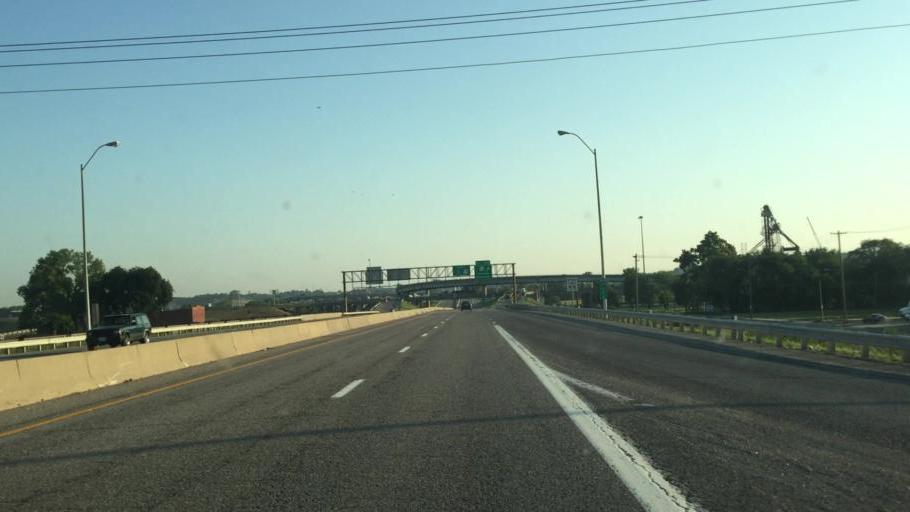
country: US
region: Kansas
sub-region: Doniphan County
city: Elwood
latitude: 39.7443
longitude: -94.8535
